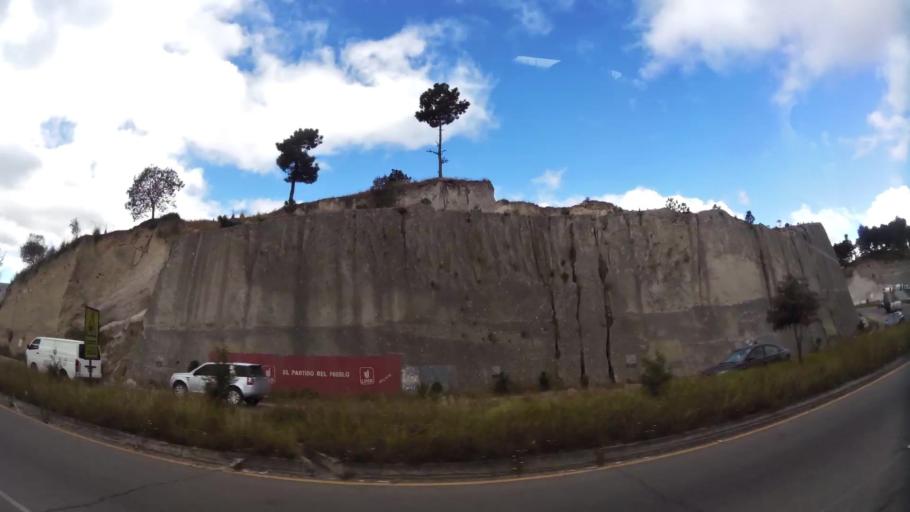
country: GT
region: Quetzaltenango
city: Salcaja
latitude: 14.8708
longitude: -91.4685
